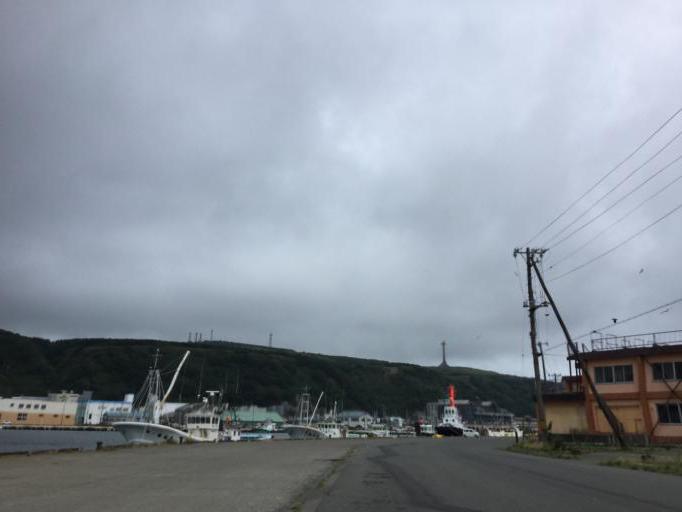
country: JP
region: Hokkaido
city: Wakkanai
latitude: 45.4051
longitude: 141.6808
